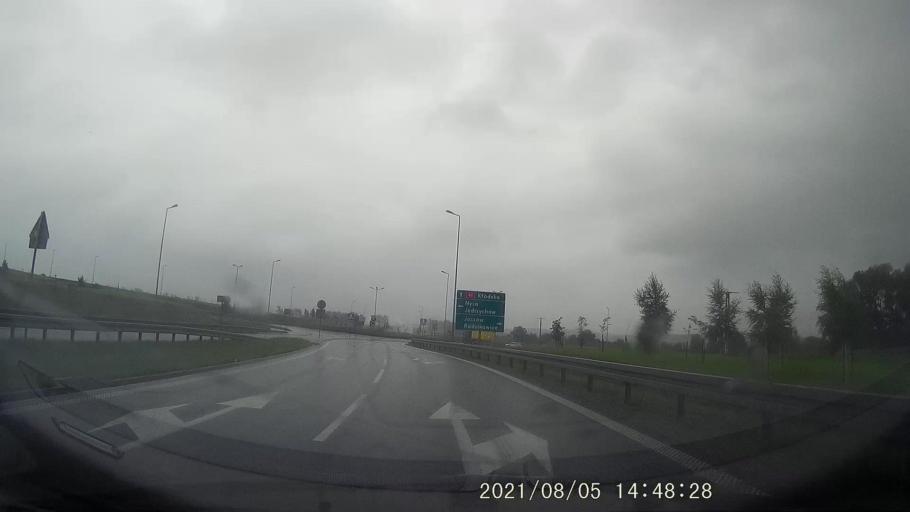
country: PL
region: Opole Voivodeship
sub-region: Powiat nyski
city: Nysa
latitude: 50.4980
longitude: 17.2907
